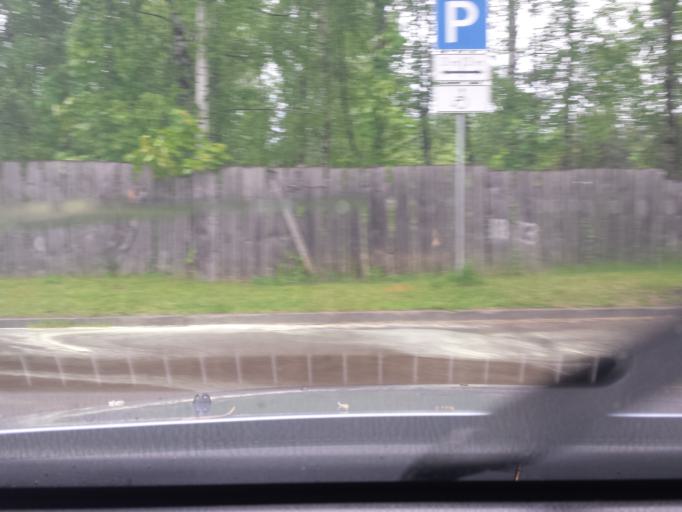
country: LV
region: Riga
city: Bolderaja
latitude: 57.0763
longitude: 24.0973
